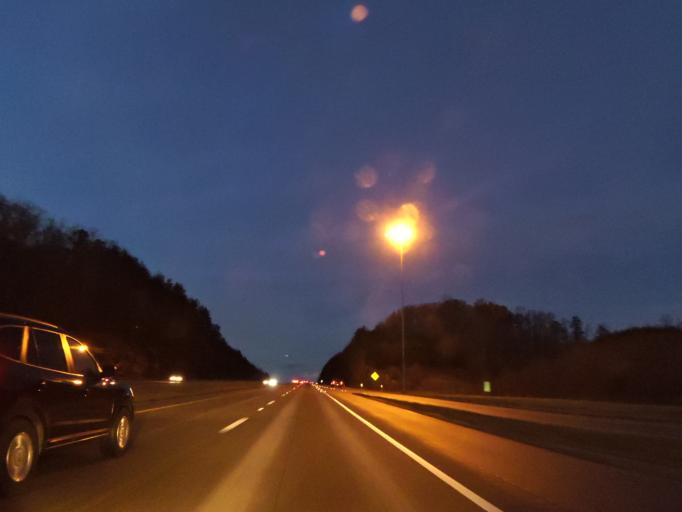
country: US
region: Kentucky
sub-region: Whitley County
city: Corbin
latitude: 36.9223
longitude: -84.1285
